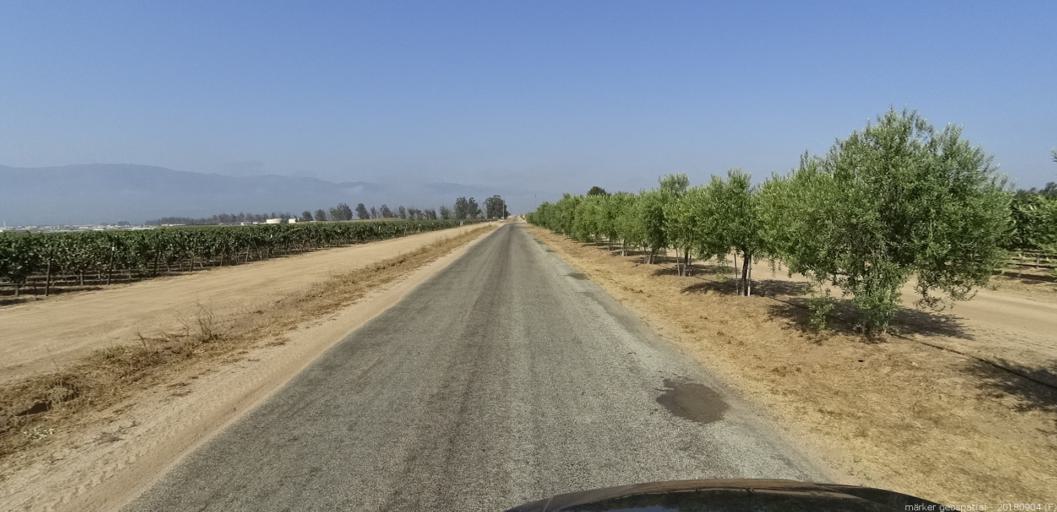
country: US
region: California
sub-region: Monterey County
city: Soledad
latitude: 36.4891
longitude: -121.3624
